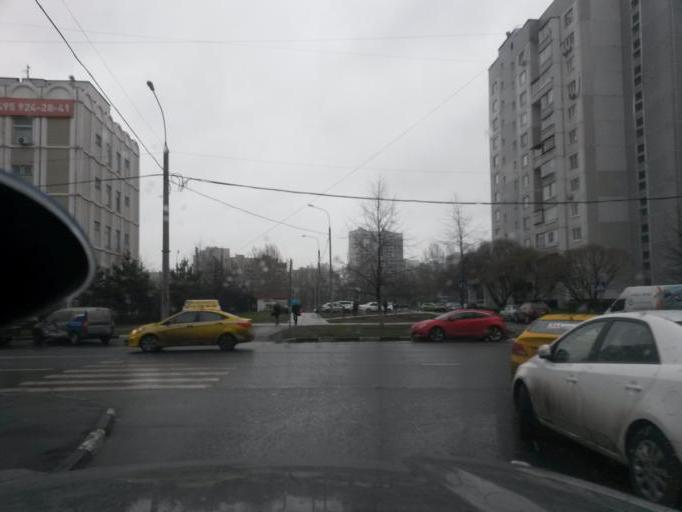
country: RU
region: Moscow
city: Brateyevo
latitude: 55.6484
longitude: 37.7522
